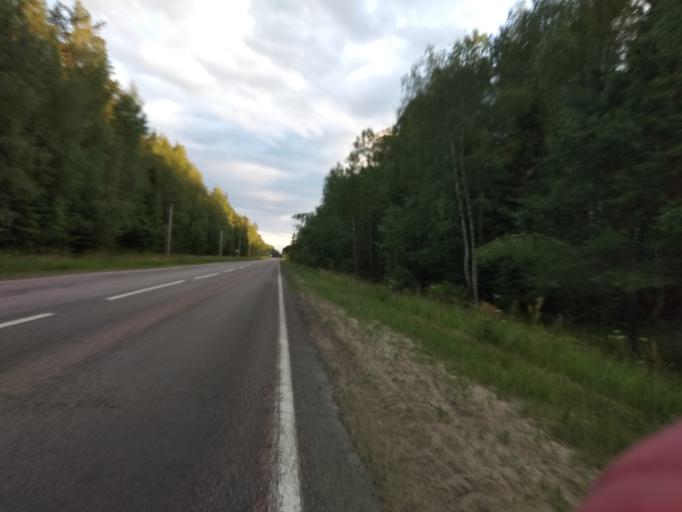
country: RU
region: Moskovskaya
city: Misheronskiy
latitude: 55.6236
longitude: 39.7324
